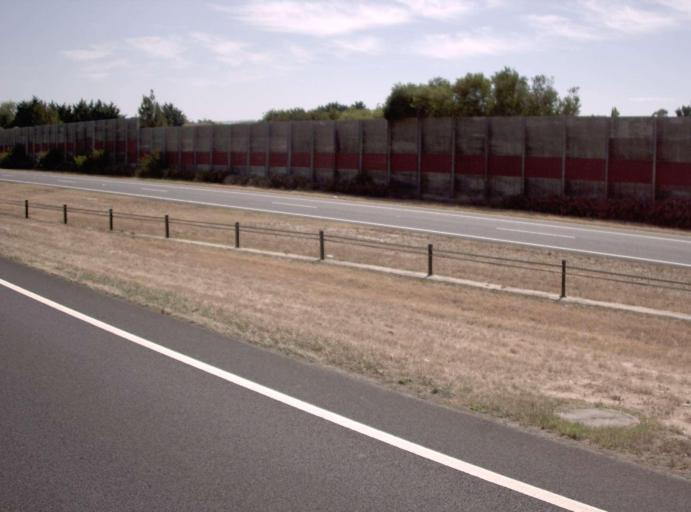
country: AU
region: Victoria
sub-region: Casey
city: Narre Warren
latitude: -38.0086
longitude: 145.3004
